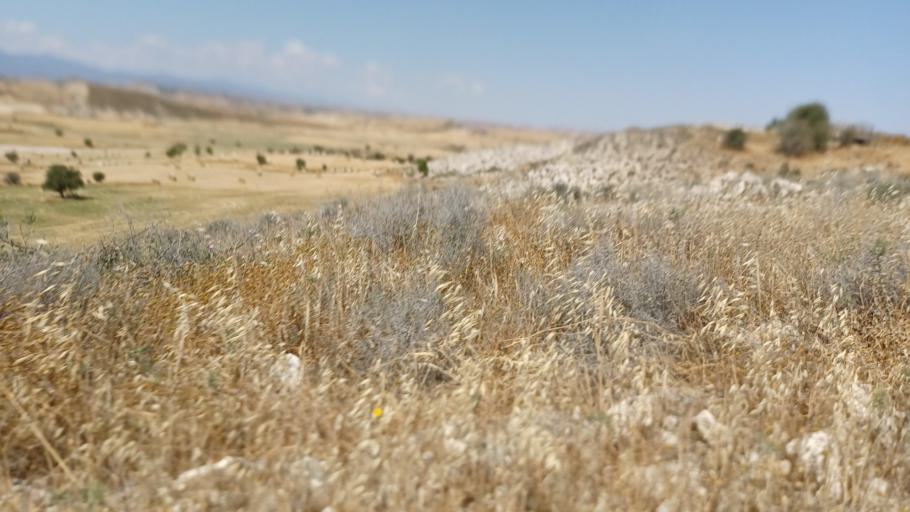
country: CY
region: Larnaka
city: Athienou
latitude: 35.0232
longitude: 33.5278
